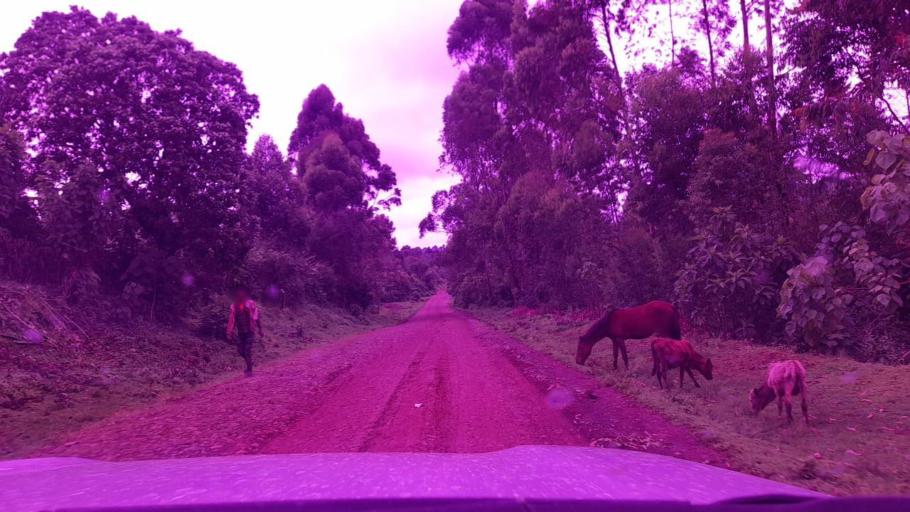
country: ET
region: Southern Nations, Nationalities, and People's Region
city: Tippi
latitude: 7.5672
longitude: 35.7865
